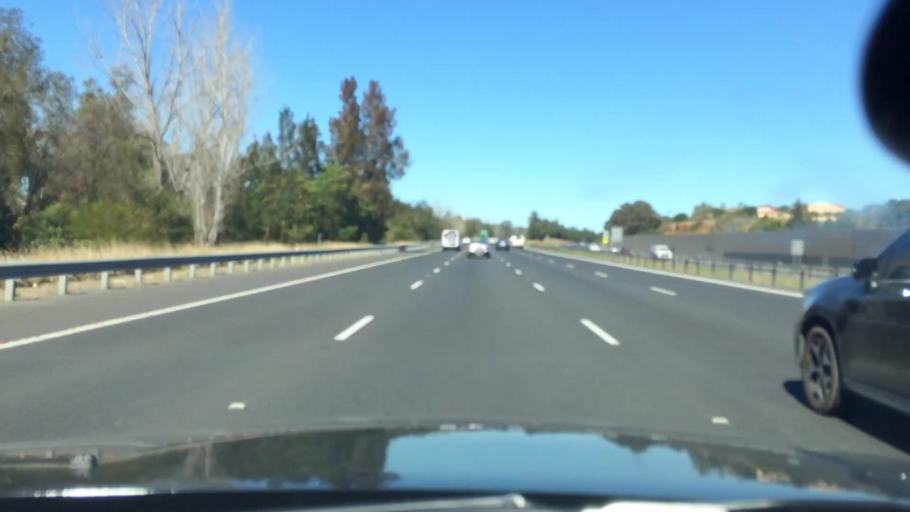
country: AU
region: New South Wales
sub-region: Campbelltown Municipality
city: Denham Court
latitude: -33.9931
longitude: 150.8517
